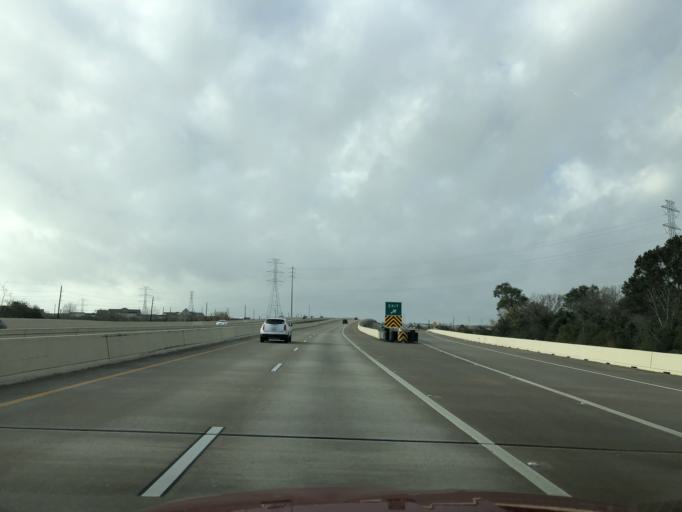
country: US
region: Texas
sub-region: Harris County
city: Katy
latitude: 29.8354
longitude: -95.7583
